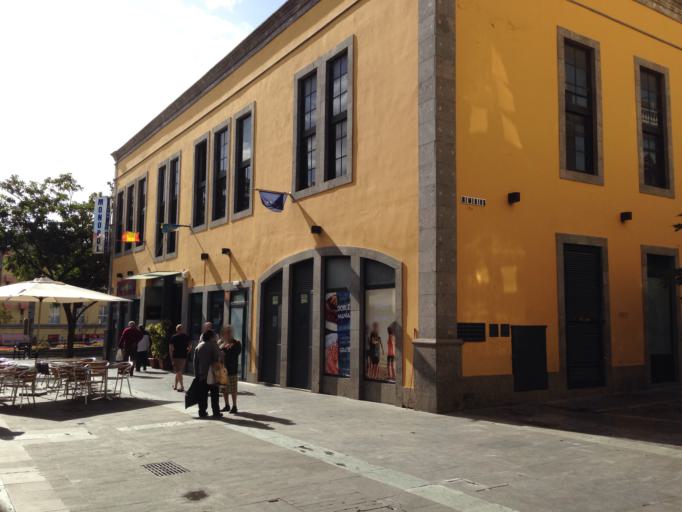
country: ES
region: Canary Islands
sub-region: Provincia de Las Palmas
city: Las Palmas de Gran Canaria
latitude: 28.1030
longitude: -15.4150
